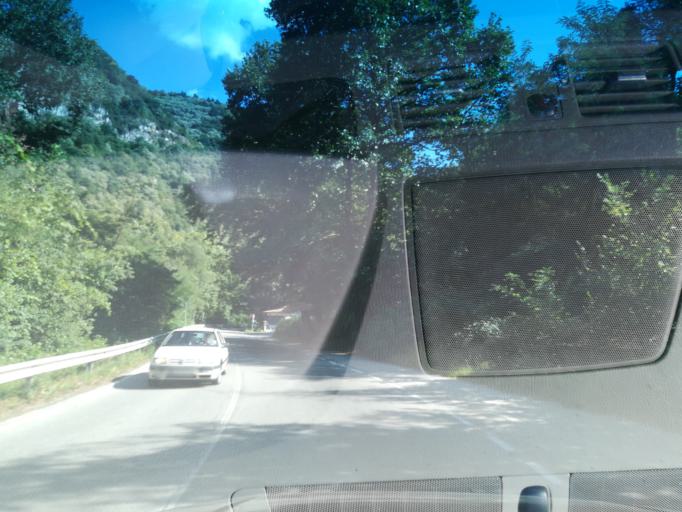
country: BG
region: Plovdiv
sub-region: Obshtina Asenovgrad
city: Asenovgrad
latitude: 41.9769
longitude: 24.8662
